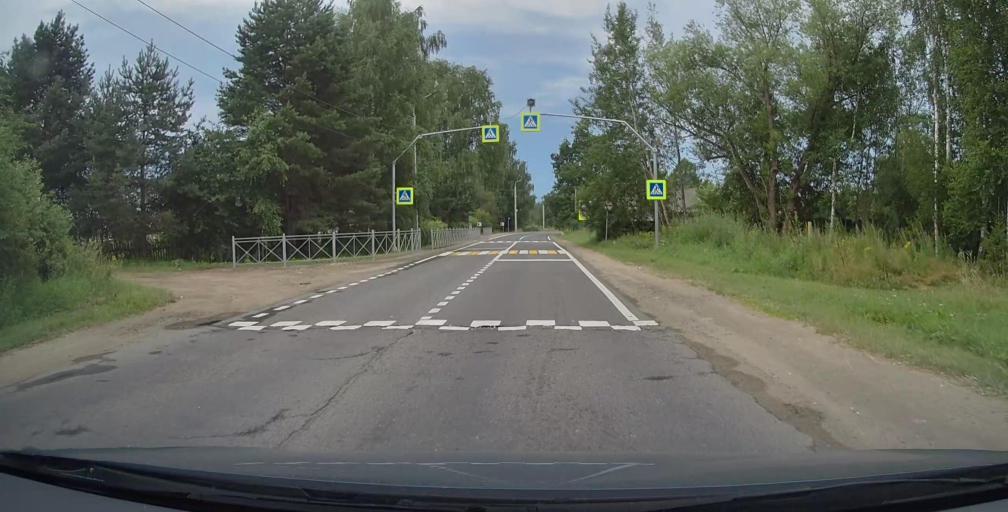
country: RU
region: Jaroslavl
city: Myshkin
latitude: 57.7992
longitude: 38.5077
